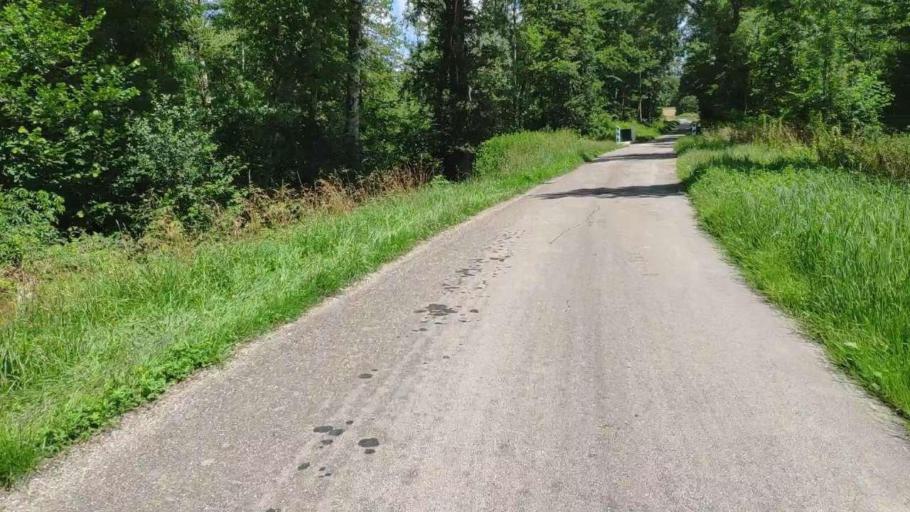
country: FR
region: Franche-Comte
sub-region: Departement du Jura
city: Chaussin
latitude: 46.8747
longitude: 5.4712
